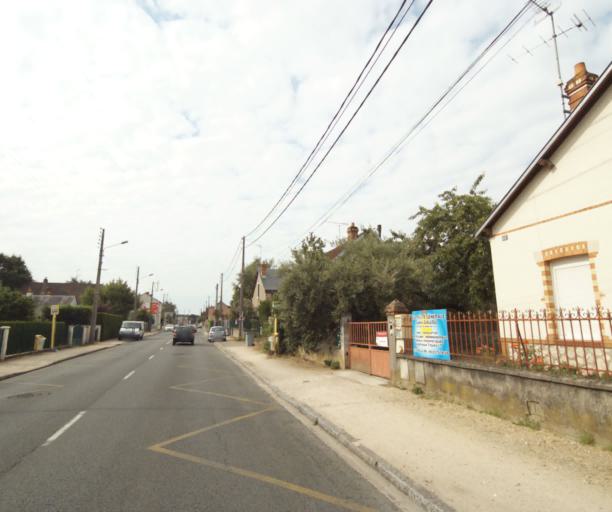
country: FR
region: Centre
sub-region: Departement du Loiret
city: Fleury-les-Aubrais
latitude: 47.9223
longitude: 1.9143
